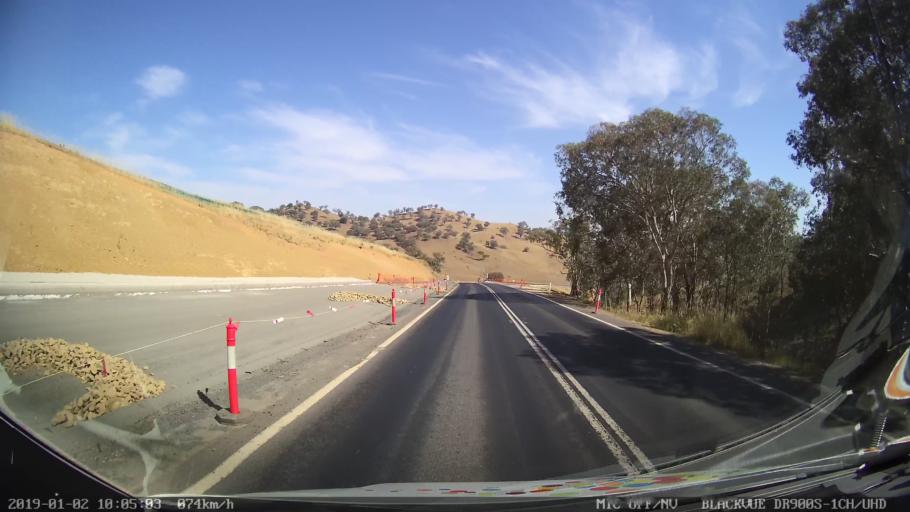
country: AU
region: New South Wales
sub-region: Gundagai
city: Gundagai
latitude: -35.1626
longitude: 148.1190
